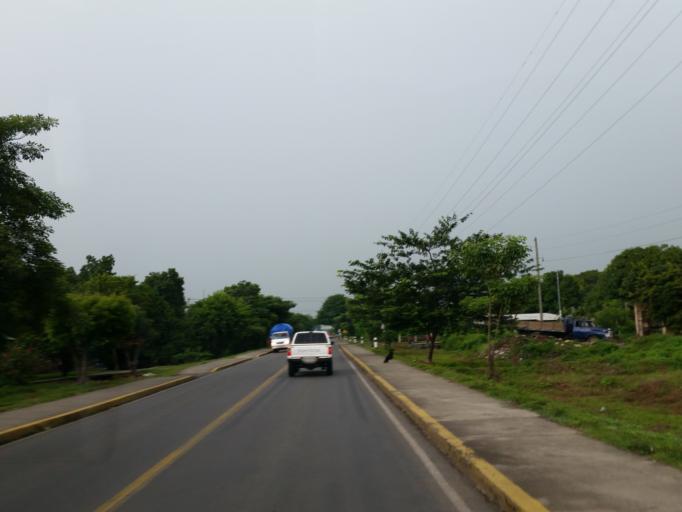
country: NI
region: Chinandega
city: Chinandega
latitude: 12.6522
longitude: -87.1242
